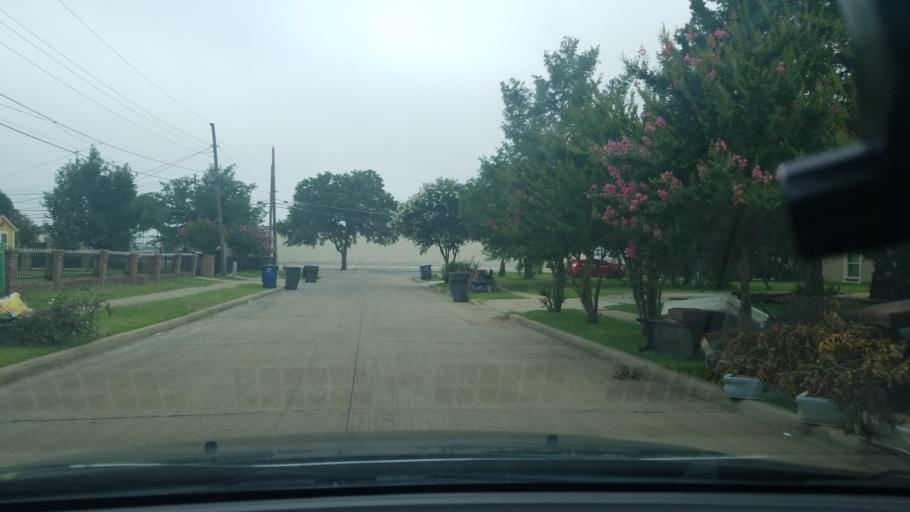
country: US
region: Texas
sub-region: Dallas County
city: Balch Springs
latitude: 32.7530
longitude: -96.6844
